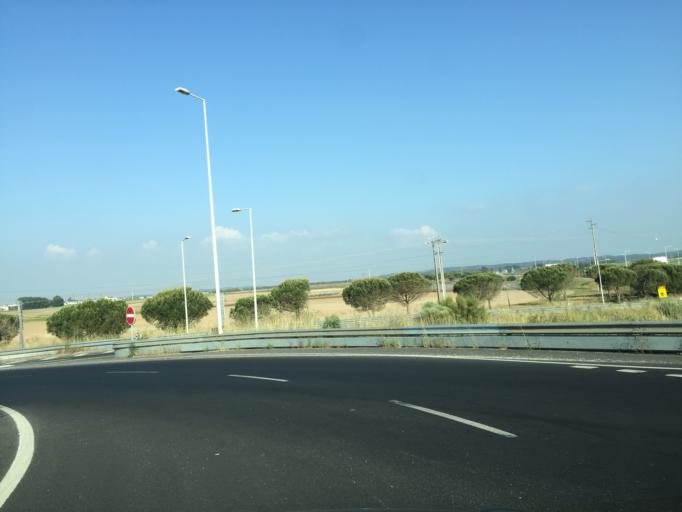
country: PT
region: Santarem
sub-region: Almeirim
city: Almeirim
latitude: 39.1907
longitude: -8.6481
